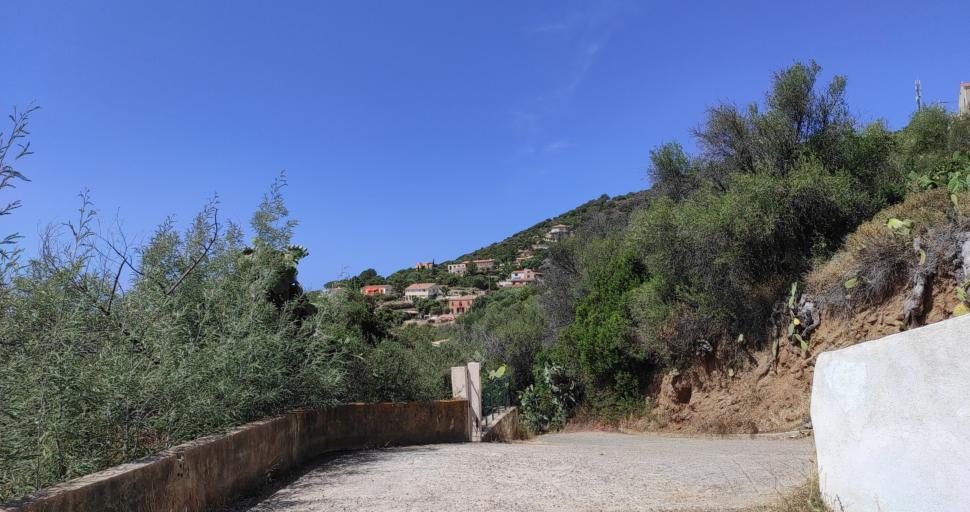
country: FR
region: Corsica
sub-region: Departement de la Corse-du-Sud
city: Cargese
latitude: 42.1330
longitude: 8.5966
